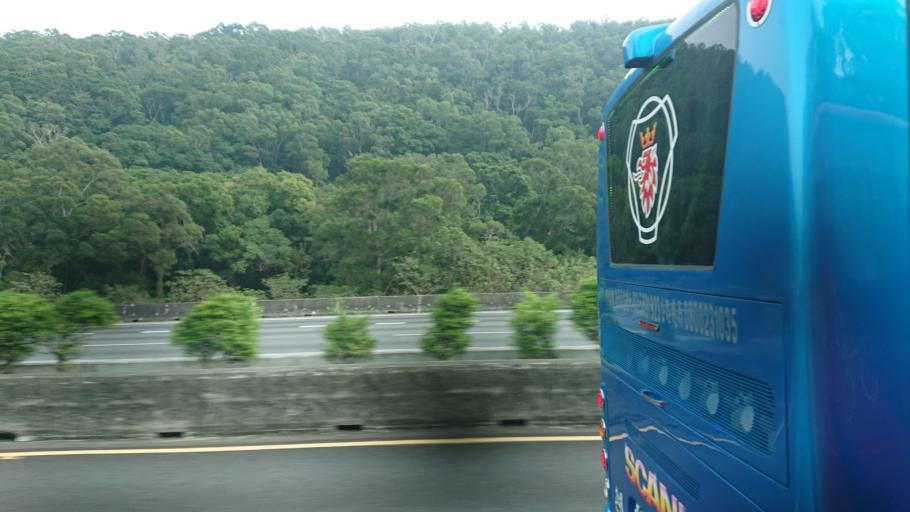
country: TW
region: Taiwan
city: Fengyuan
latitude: 24.3702
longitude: 120.7460
